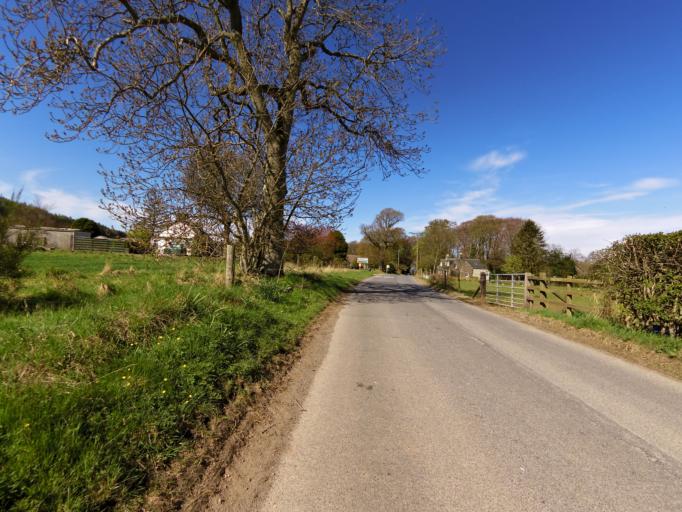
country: GB
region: Scotland
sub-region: Dundee City
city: Dundee
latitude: 56.4081
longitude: -3.0226
